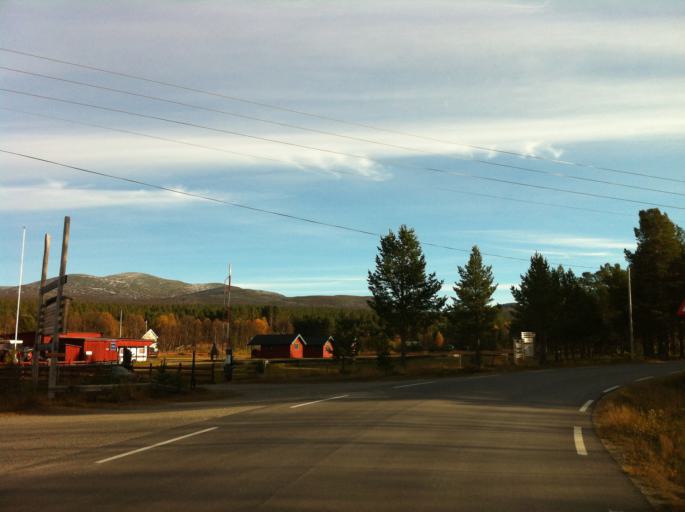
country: NO
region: Hedmark
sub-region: Engerdal
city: Engerdal
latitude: 62.1670
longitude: 11.9423
